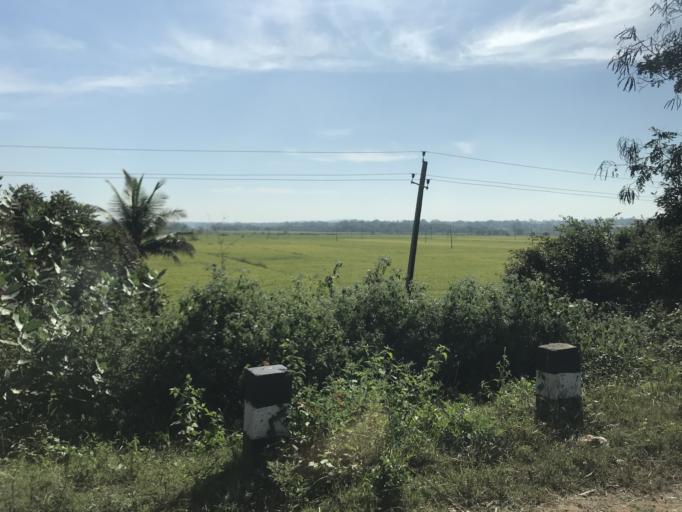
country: IN
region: Karnataka
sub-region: Mysore
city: Heggadadevankote
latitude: 12.1228
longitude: 76.4238
